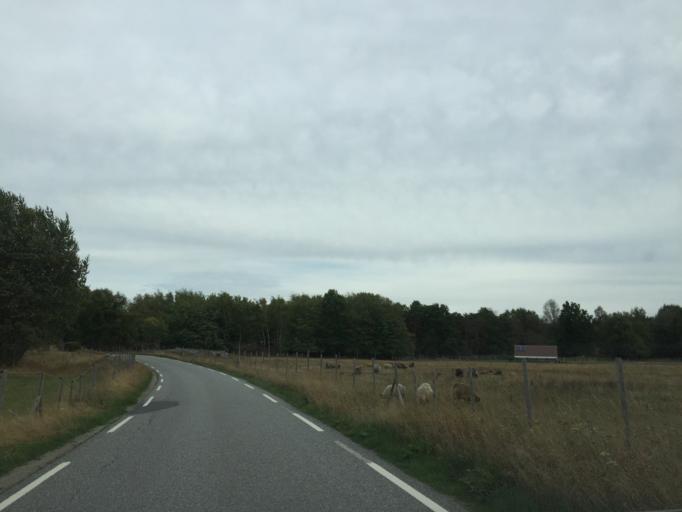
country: NO
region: Ostfold
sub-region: Hvaler
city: Skjaerhalden
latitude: 59.0402
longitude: 11.0353
